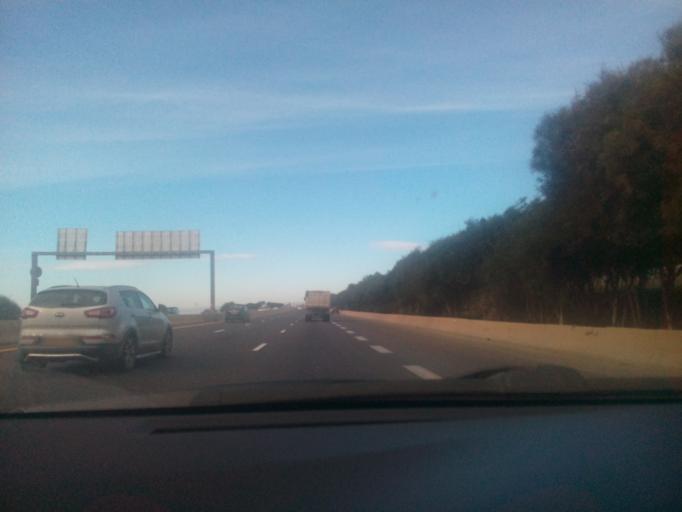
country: DZ
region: Oran
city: Sidi ech Chahmi
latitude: 35.5763
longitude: -0.5603
